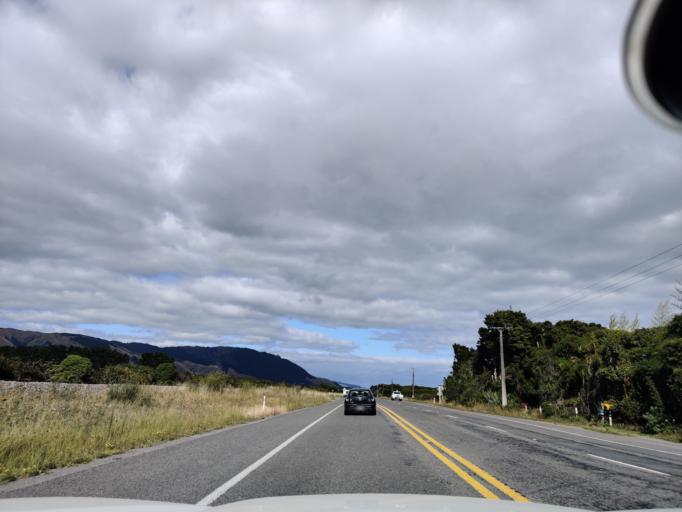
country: NZ
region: Wellington
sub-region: Kapiti Coast District
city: Otaki
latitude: -40.7889
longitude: 175.1320
